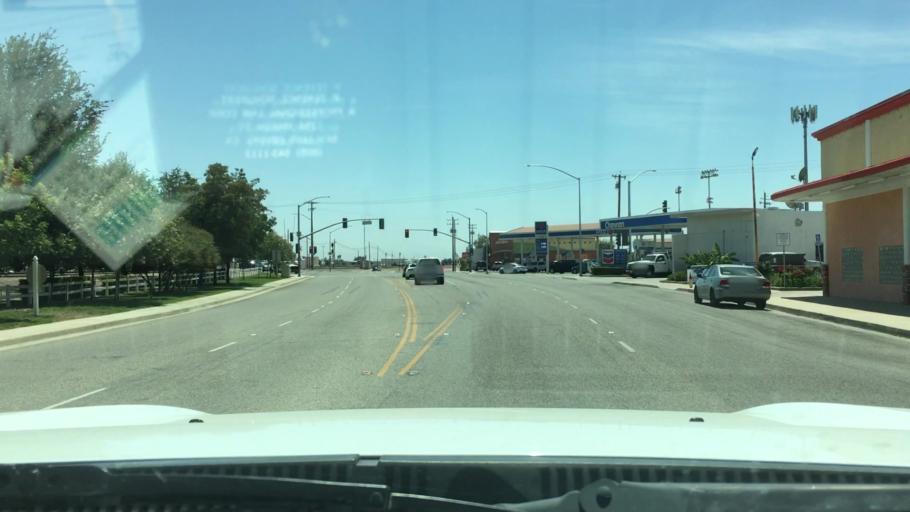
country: US
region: California
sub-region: Kern County
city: Shafter
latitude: 35.5005
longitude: -119.2716
